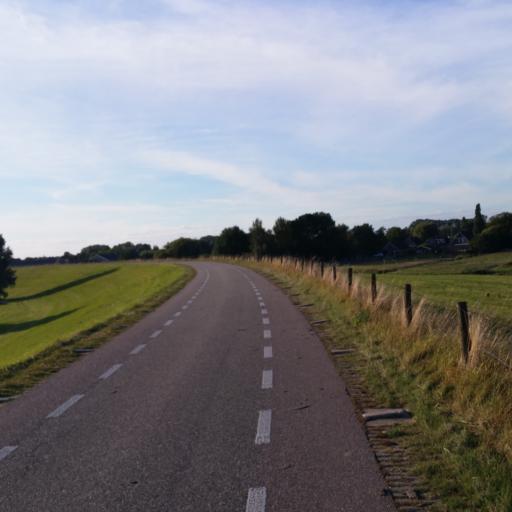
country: NL
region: Utrecht
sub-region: Gemeente IJsselstein
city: IJsselstein
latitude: 51.9798
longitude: 5.0150
